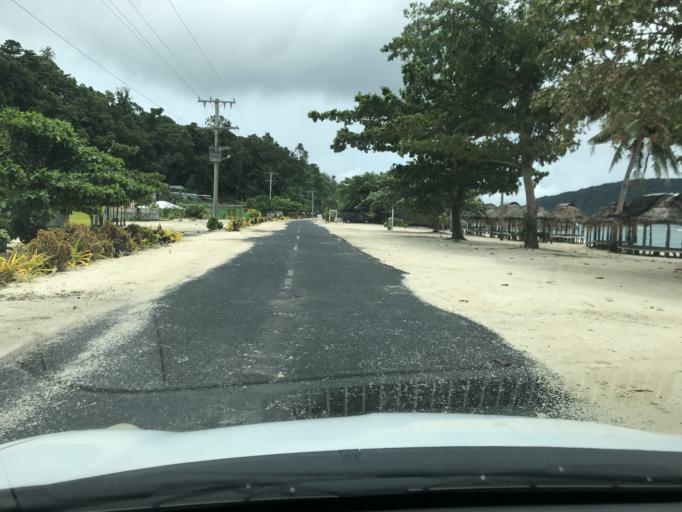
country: WS
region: Va`a-o-Fonoti
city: Samamea
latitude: -14.0457
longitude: -171.4476
